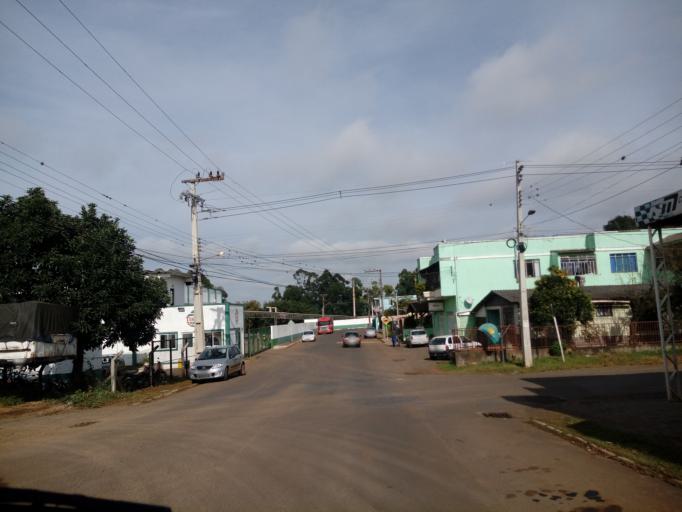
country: BR
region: Santa Catarina
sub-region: Chapeco
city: Chapeco
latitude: -27.0989
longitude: -52.6323
